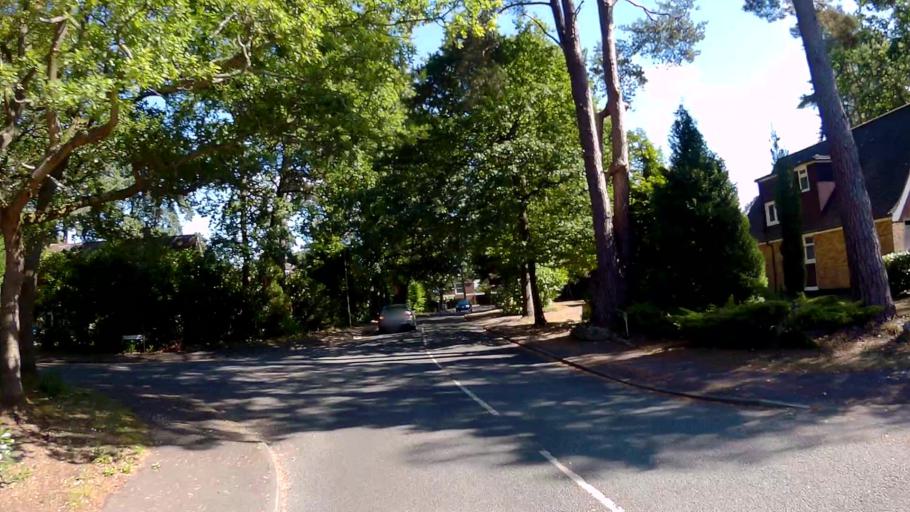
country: GB
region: England
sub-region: Bracknell Forest
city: Crowthorne
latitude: 51.3738
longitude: -0.8055
